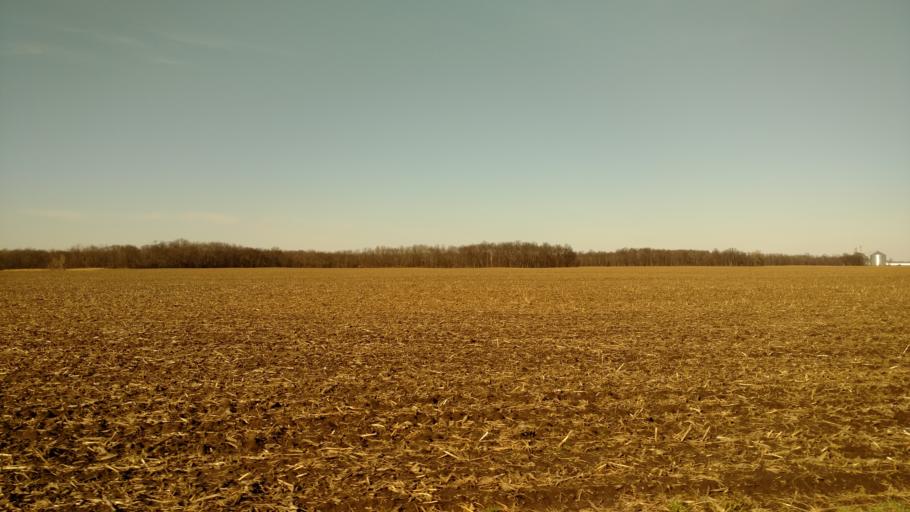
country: US
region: Ohio
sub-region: Crawford County
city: Bucyrus
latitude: 40.7031
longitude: -83.0559
